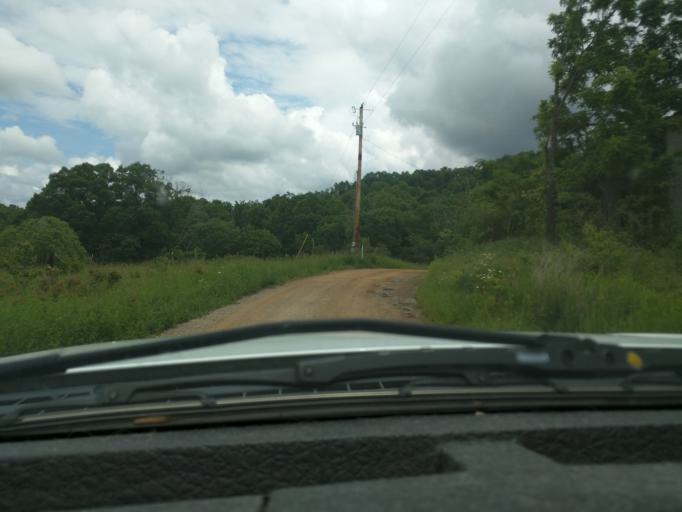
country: US
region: Arkansas
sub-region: Madison County
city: Huntsville
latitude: 35.8832
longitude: -93.5460
